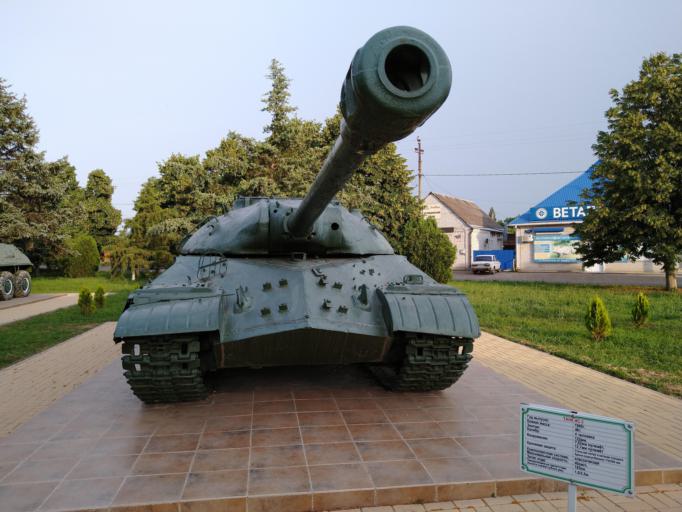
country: RU
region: Krasnodarskiy
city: Kavkazskaya
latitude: 45.4360
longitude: 40.6502
